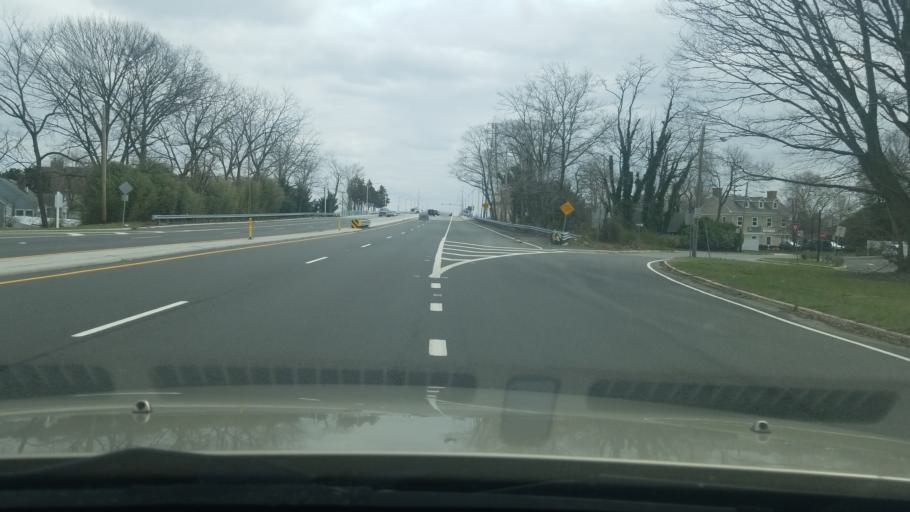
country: US
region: New Jersey
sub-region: Monmouth County
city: Brielle
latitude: 40.1076
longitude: -74.0562
